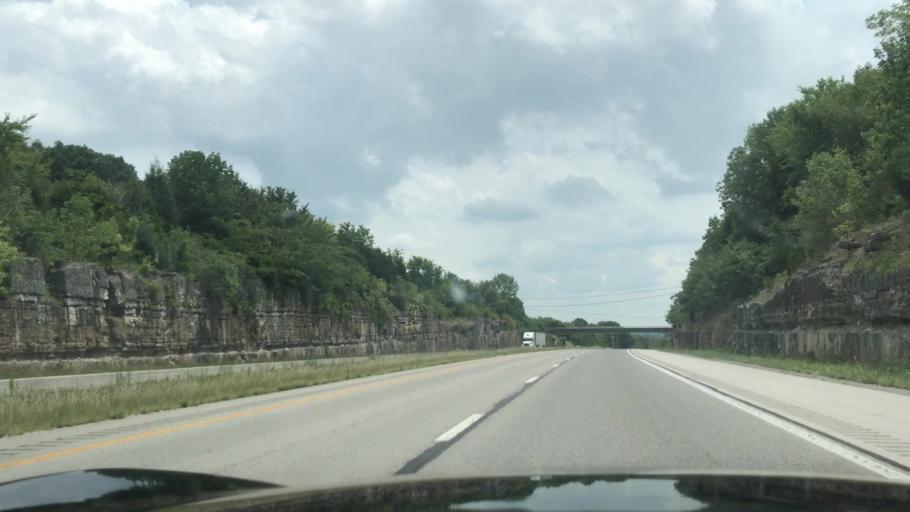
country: US
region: Kentucky
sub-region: Warren County
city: Bowling Green
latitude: 37.0047
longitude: -86.5078
